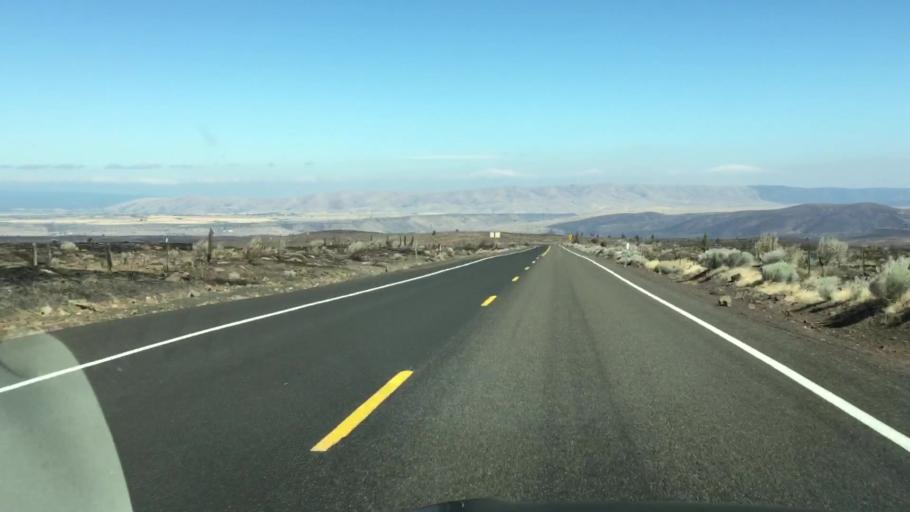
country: US
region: Oregon
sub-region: Jefferson County
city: Warm Springs
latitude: 45.1045
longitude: -121.0397
